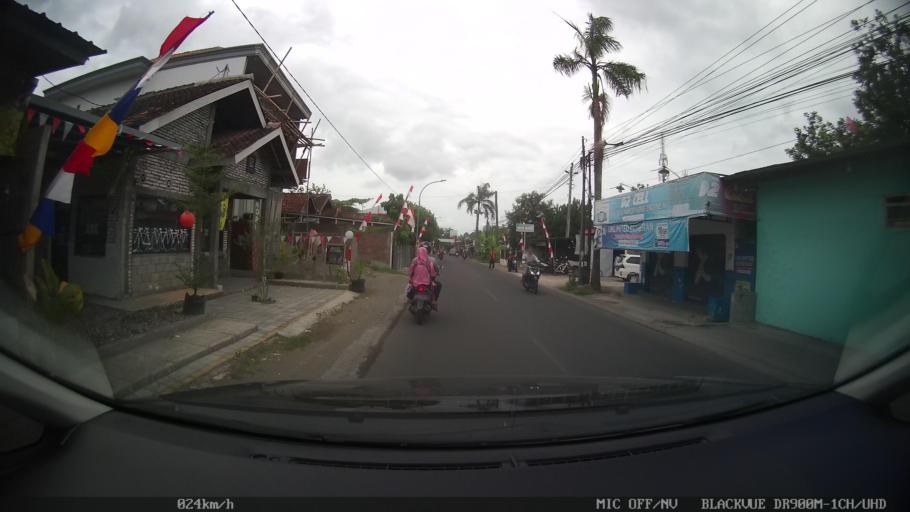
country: ID
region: Daerah Istimewa Yogyakarta
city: Sewon
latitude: -7.8617
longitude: 110.4088
